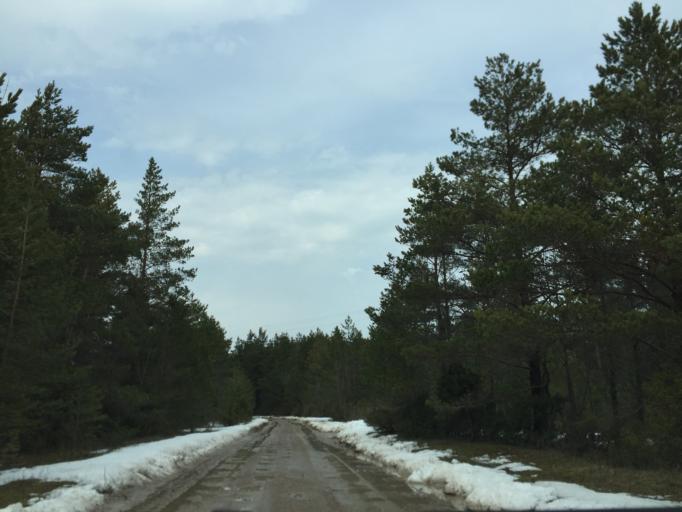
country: EE
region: Saare
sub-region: Kuressaare linn
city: Kuressaare
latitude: 58.4293
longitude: 22.1445
